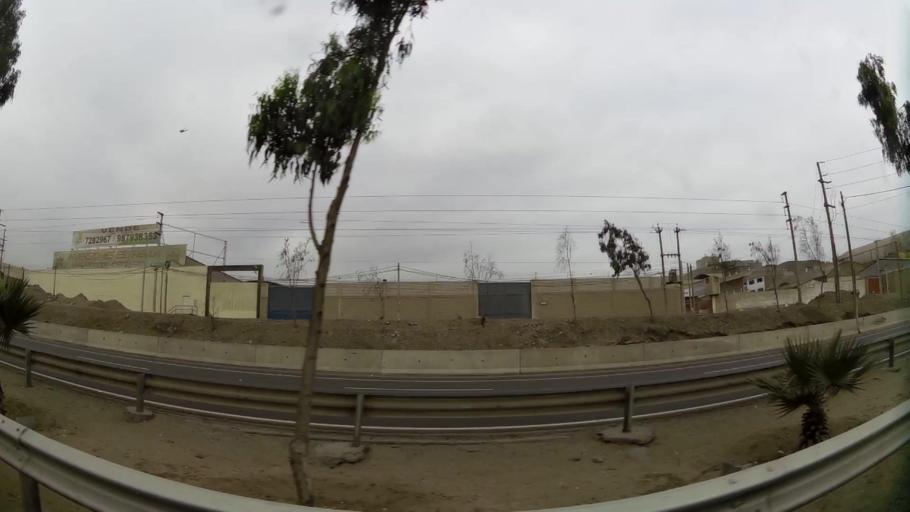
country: PE
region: Lima
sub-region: Lima
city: Surco
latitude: -12.2037
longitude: -76.9744
